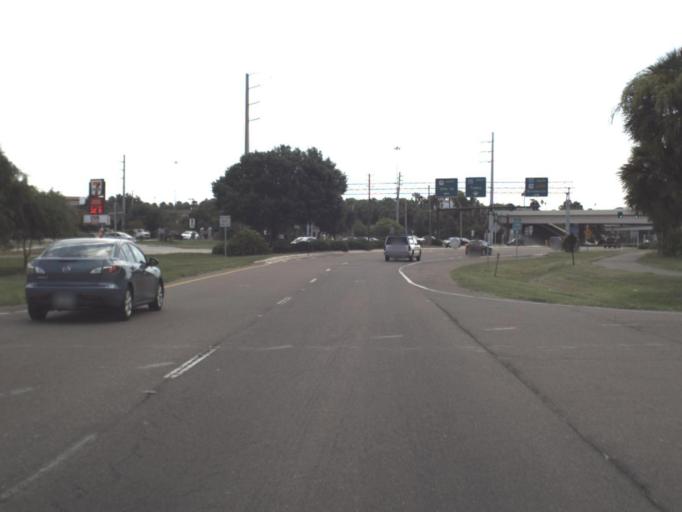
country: US
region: Florida
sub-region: Pinellas County
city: Gulfport
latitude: 27.7187
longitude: -82.6812
